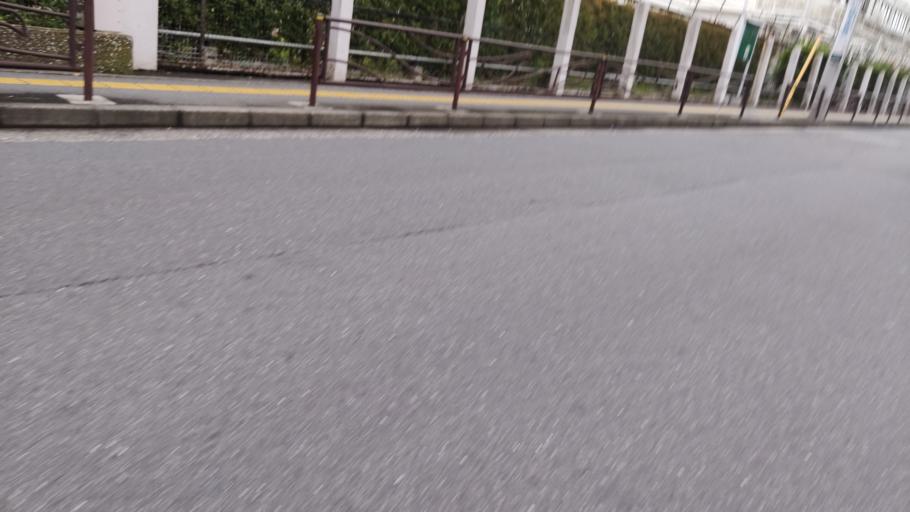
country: JP
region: Kanagawa
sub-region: Kawasaki-shi
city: Kawasaki
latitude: 35.5816
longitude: 139.6417
